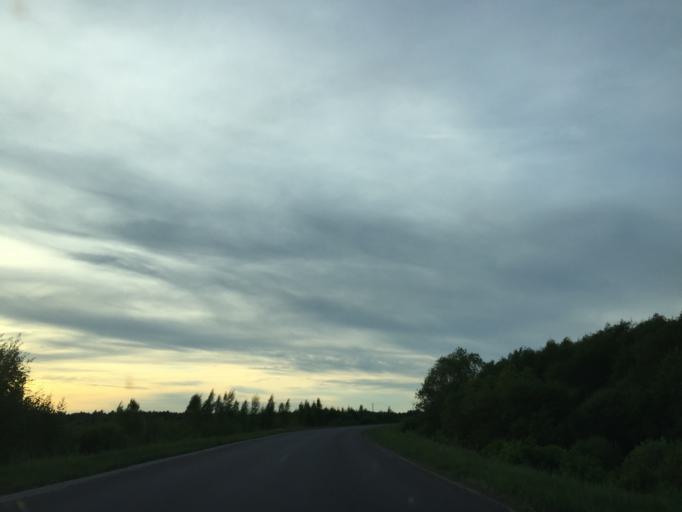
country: LV
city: Tireli
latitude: 56.8134
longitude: 23.5728
